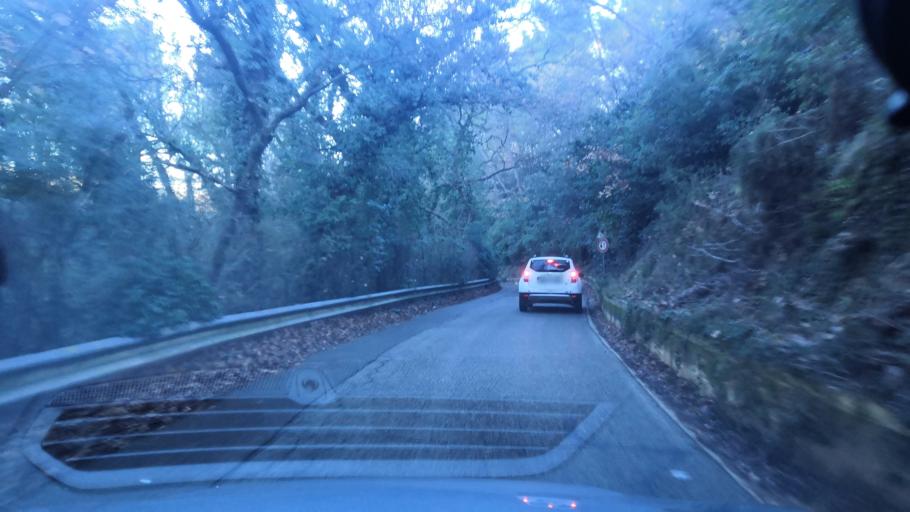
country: FR
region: Provence-Alpes-Cote d'Azur
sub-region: Departement des Bouches-du-Rhone
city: Aix-en-Provence
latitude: 43.5185
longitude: 5.4123
